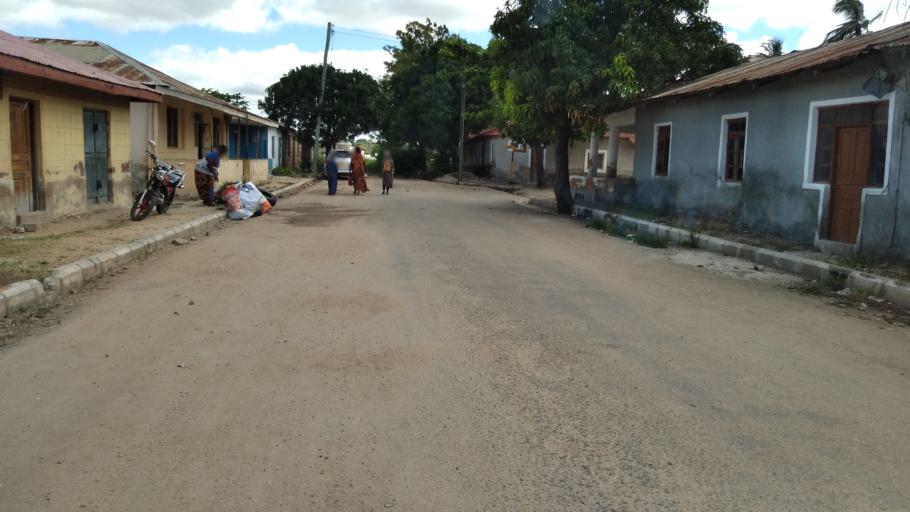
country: TZ
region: Dodoma
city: Dodoma
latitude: -6.1722
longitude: 35.7501
